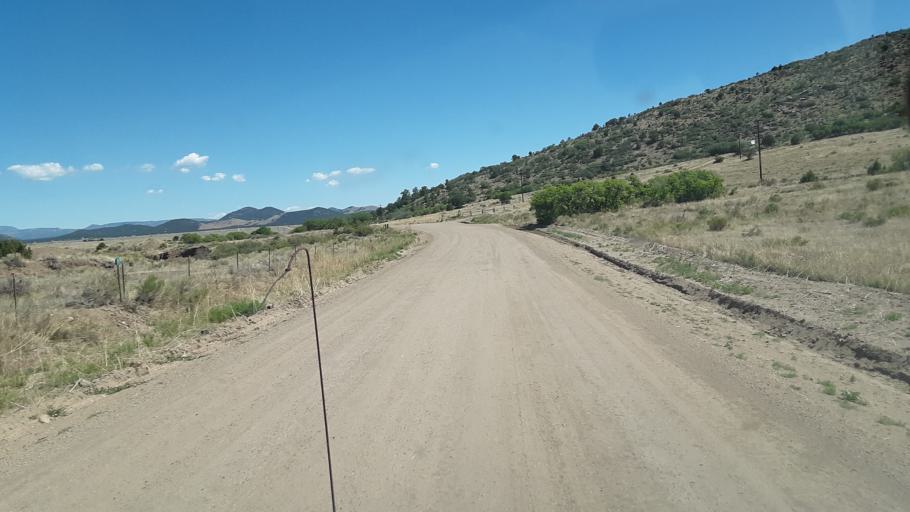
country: US
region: Colorado
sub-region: Custer County
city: Westcliffe
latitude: 38.2407
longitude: -105.5014
